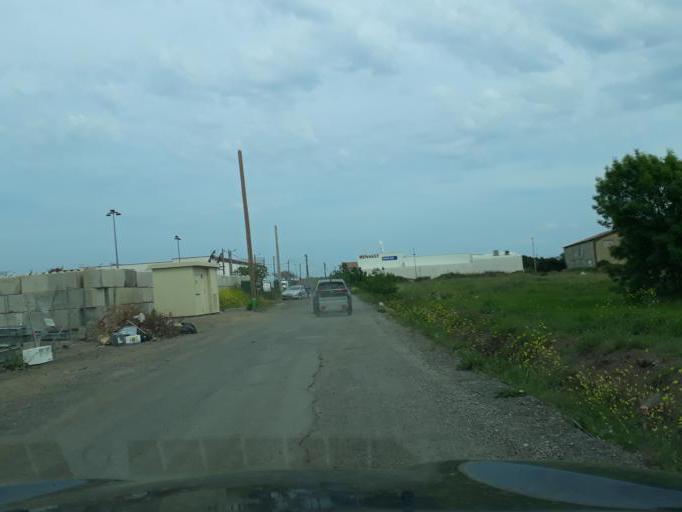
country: FR
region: Languedoc-Roussillon
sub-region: Departement de l'Herault
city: Agde
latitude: 43.2953
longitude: 3.4675
